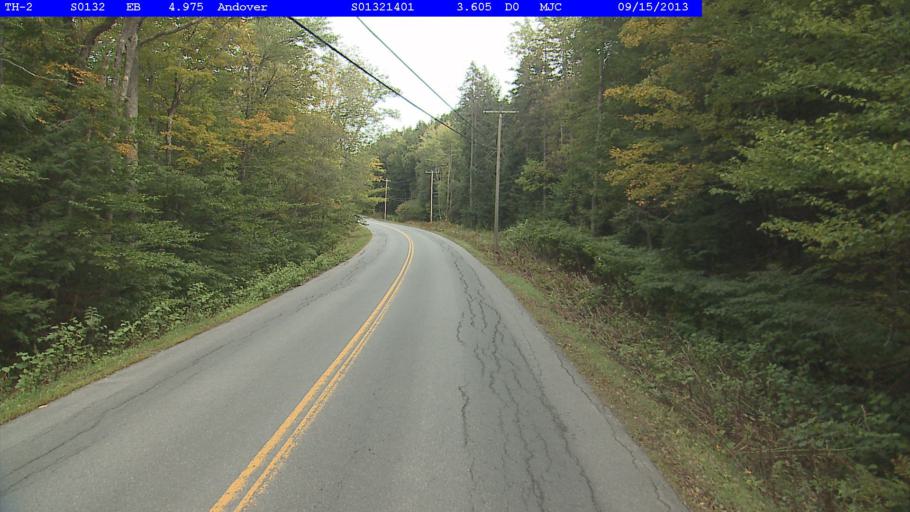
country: US
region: Vermont
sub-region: Windsor County
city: Chester
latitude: 43.2783
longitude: -72.7048
